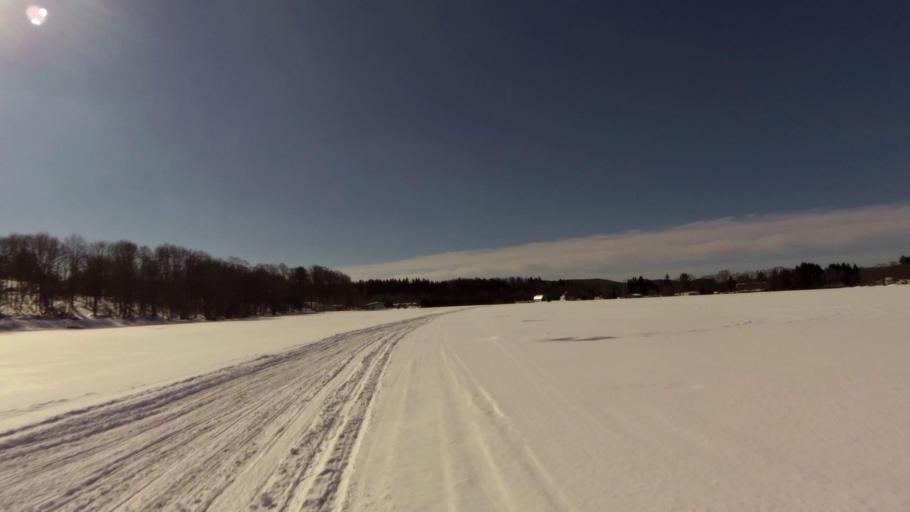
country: US
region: New York
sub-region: Cattaraugus County
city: Franklinville
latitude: 42.3483
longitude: -78.4482
